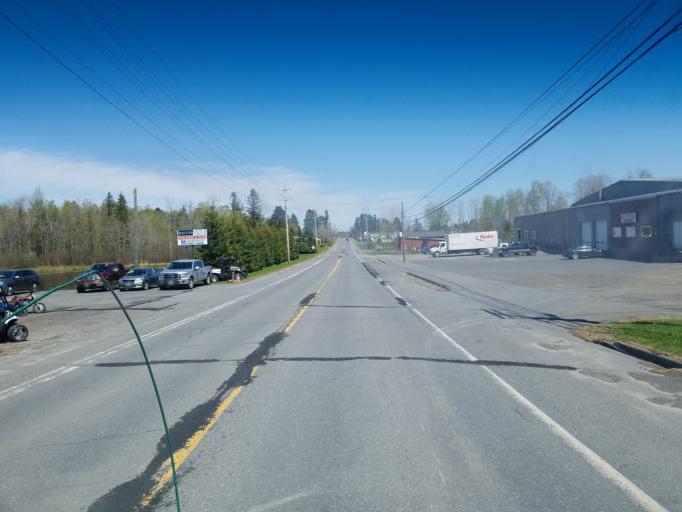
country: US
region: Maine
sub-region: Aroostook County
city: Caribou
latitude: 46.8542
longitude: -68.0298
